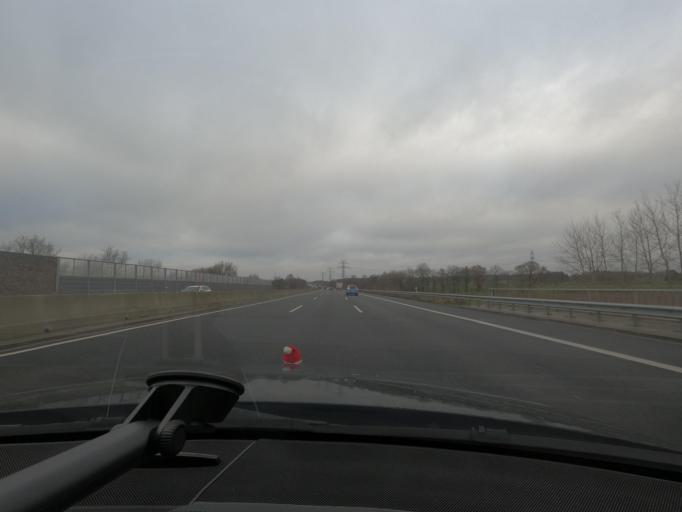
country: DE
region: Schleswig-Holstein
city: Ellerau
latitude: 53.7635
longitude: 9.9488
